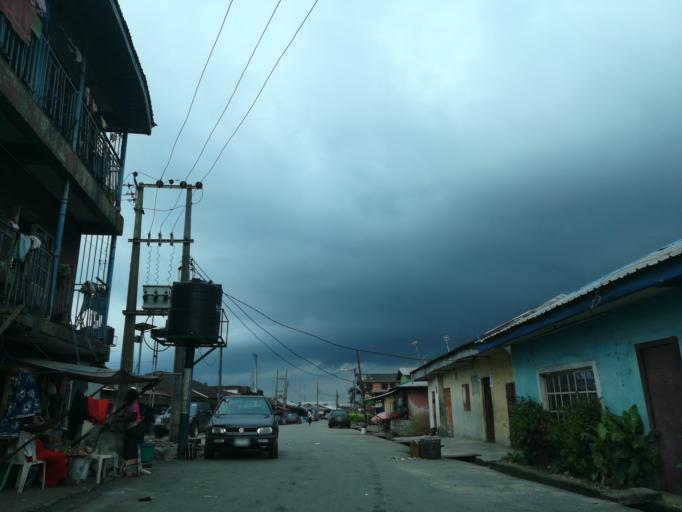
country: NG
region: Rivers
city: Port Harcourt
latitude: 4.7973
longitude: 6.9850
